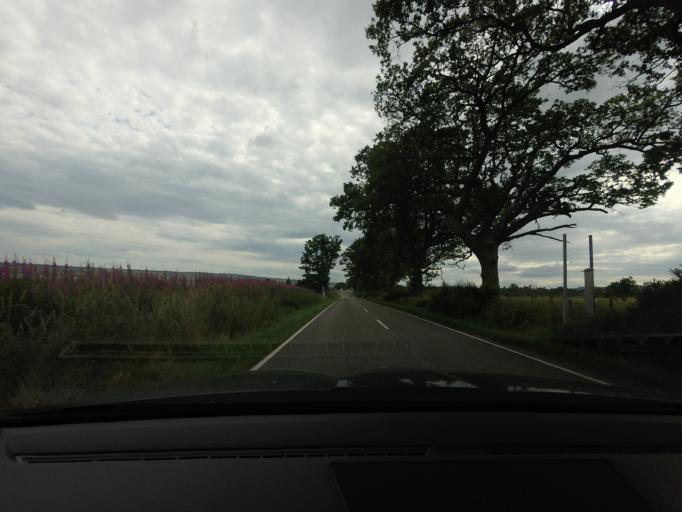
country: GB
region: Scotland
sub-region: Highland
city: Alness
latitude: 57.6863
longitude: -4.2944
